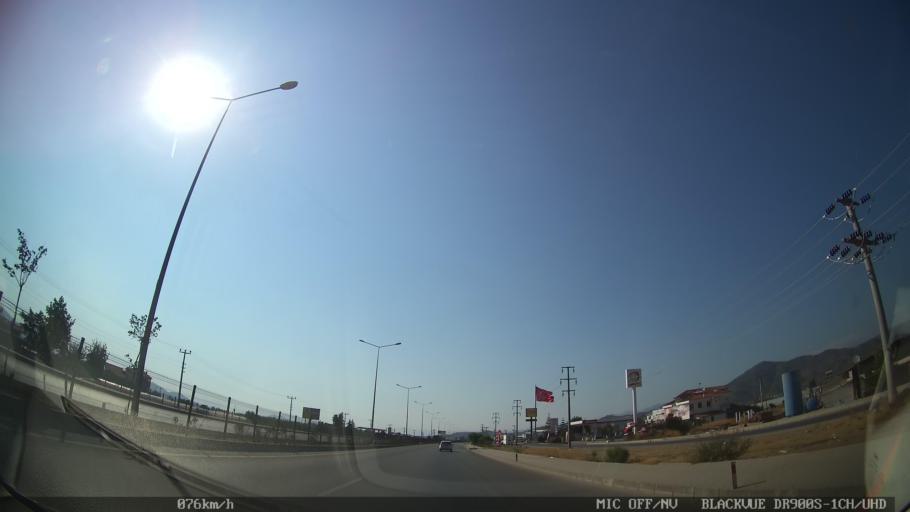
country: TR
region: Mugla
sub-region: Fethiye
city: Fethiye
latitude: 36.6560
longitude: 29.1620
